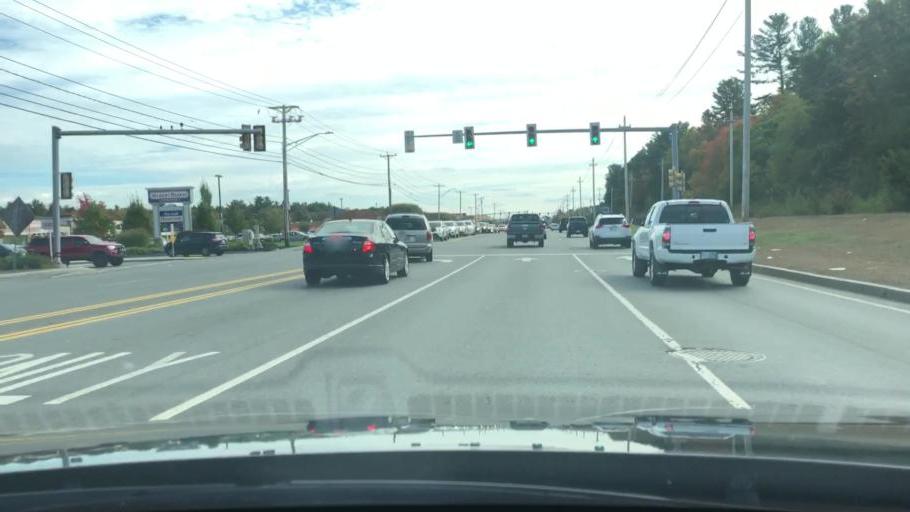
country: US
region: New Hampshire
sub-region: Rockingham County
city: Salem
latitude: 42.7631
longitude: -71.2159
